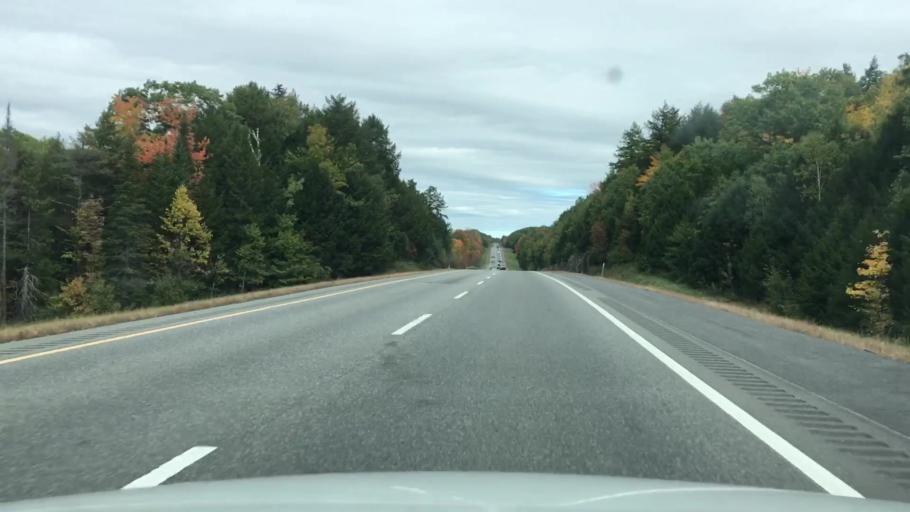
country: US
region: Maine
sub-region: Kennebec County
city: Sidney
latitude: 44.3965
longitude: -69.7546
